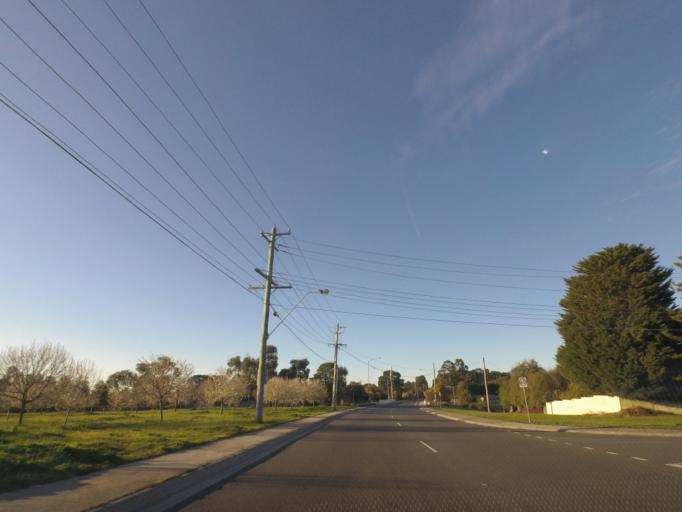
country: AU
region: Victoria
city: Mitcham
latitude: -37.8014
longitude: 145.1916
